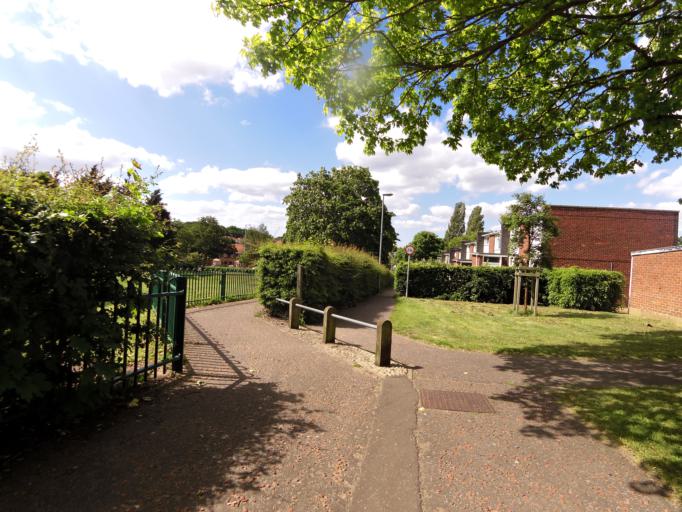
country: GB
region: England
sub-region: Norfolk
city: Norwich
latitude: 52.6534
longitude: 1.2692
